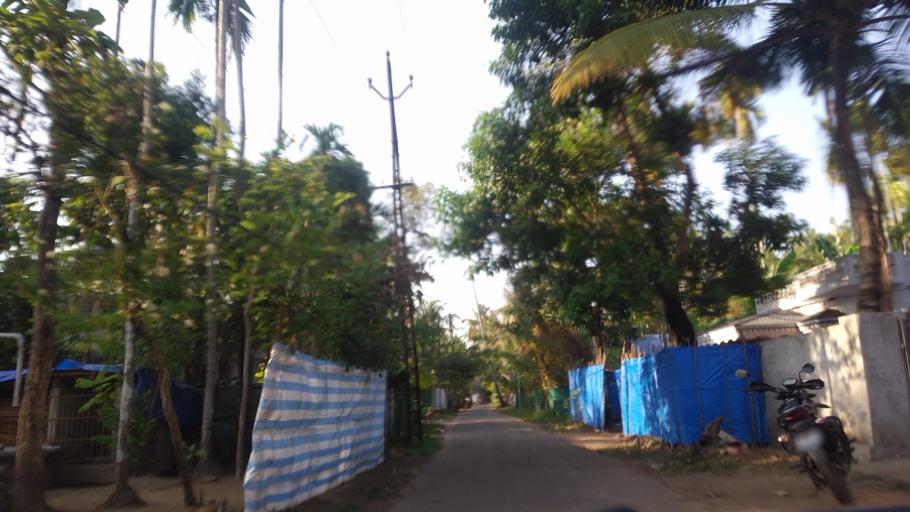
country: IN
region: Kerala
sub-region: Thrissur District
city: Kodungallur
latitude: 10.1375
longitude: 76.2021
